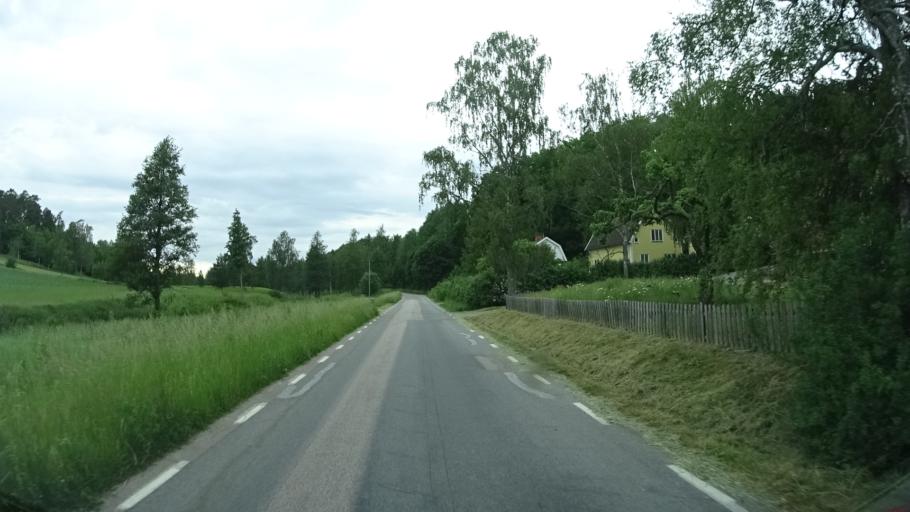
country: SE
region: Soedermanland
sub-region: Nykopings Kommun
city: Stigtomta
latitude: 58.7531
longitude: 16.7230
